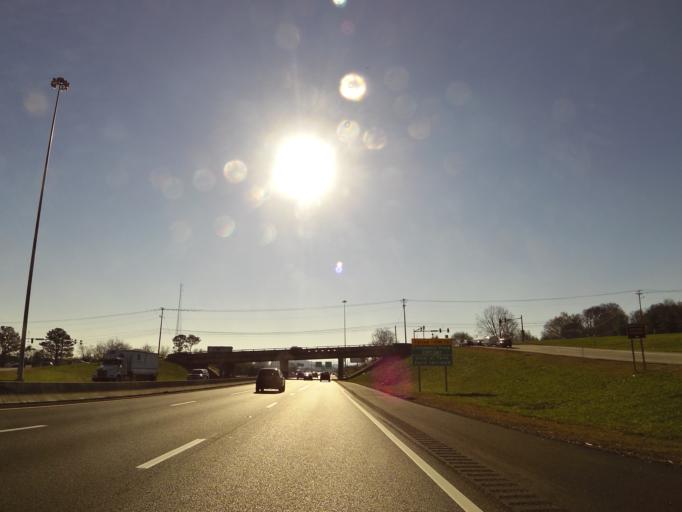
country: US
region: Tennessee
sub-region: Knox County
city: Knoxville
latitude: 35.9779
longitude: -83.9360
